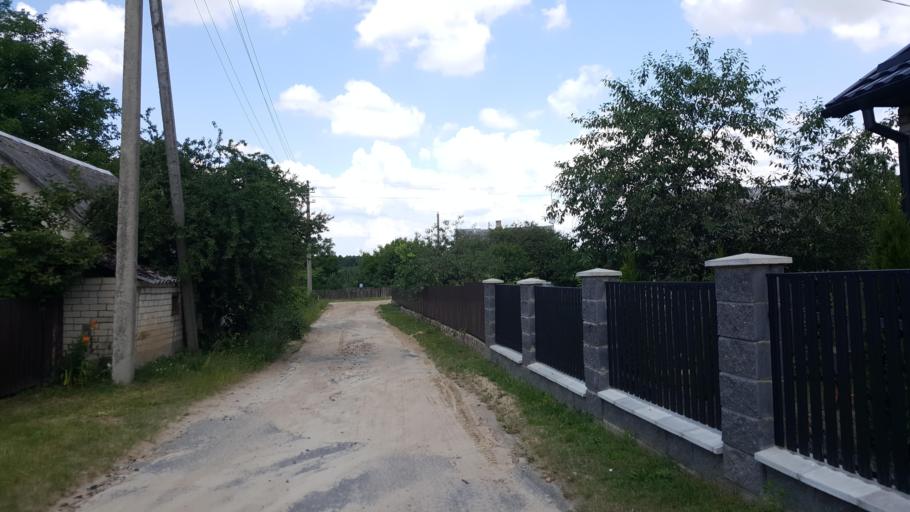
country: BY
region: Brest
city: Kamyanyets
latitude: 52.4050
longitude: 23.8301
